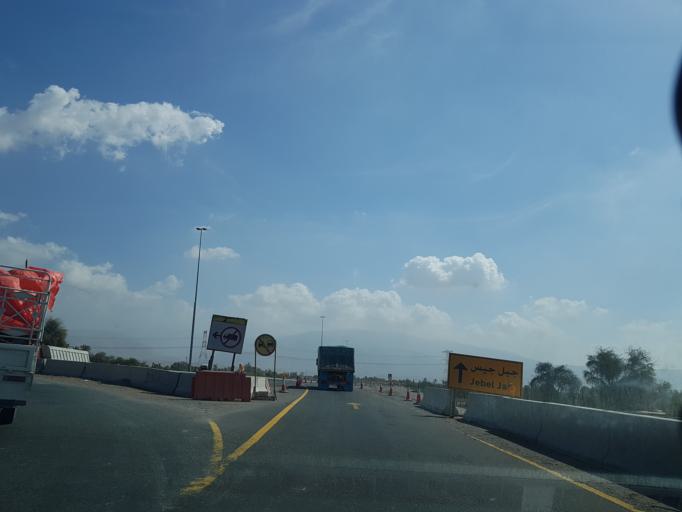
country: AE
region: Ra's al Khaymah
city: Ras al-Khaimah
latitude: 25.6981
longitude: 55.9725
